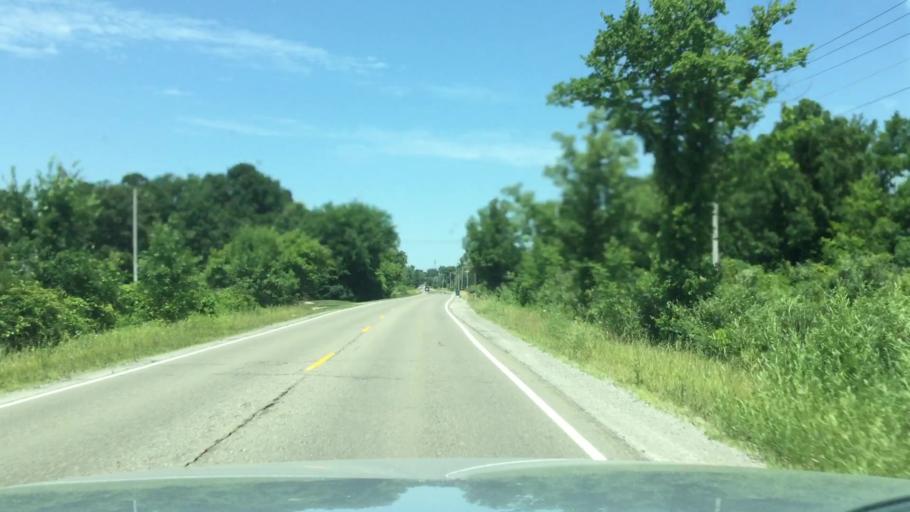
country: US
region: Michigan
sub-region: Genesee County
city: Swartz Creek
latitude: 42.9485
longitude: -83.8109
